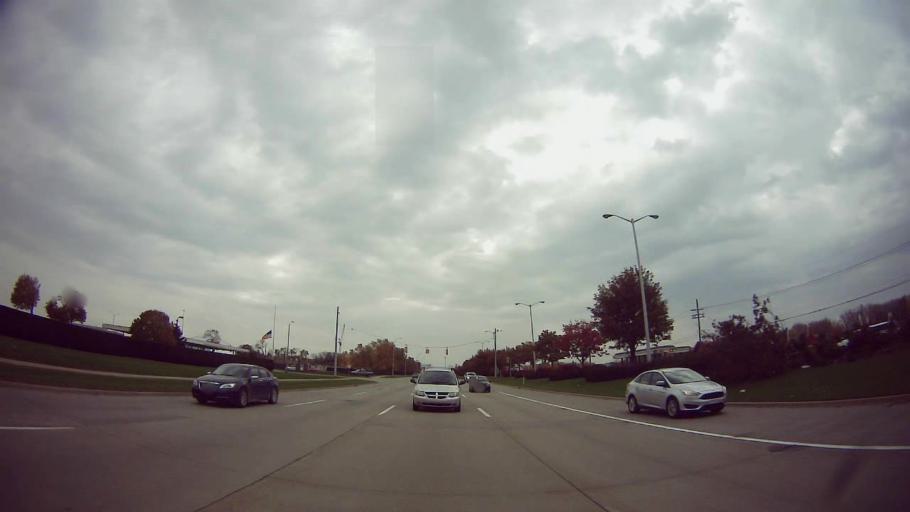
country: US
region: Michigan
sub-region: Macomb County
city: Center Line
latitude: 42.5125
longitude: -83.0465
